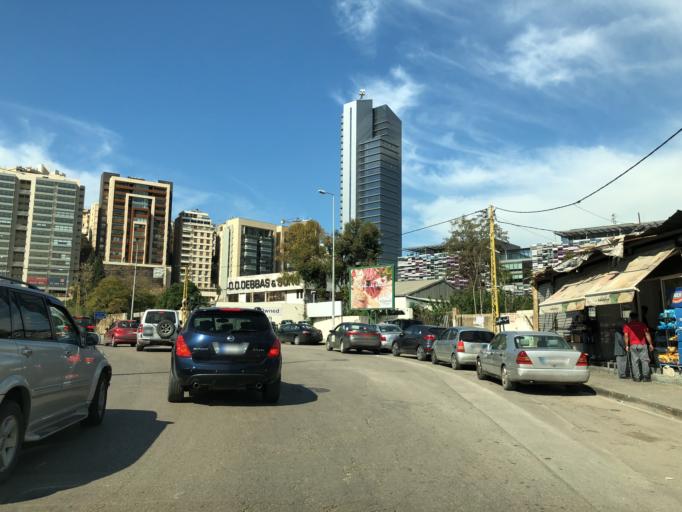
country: LB
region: Mont-Liban
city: Jdaidet el Matn
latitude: 33.8836
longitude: 35.5315
